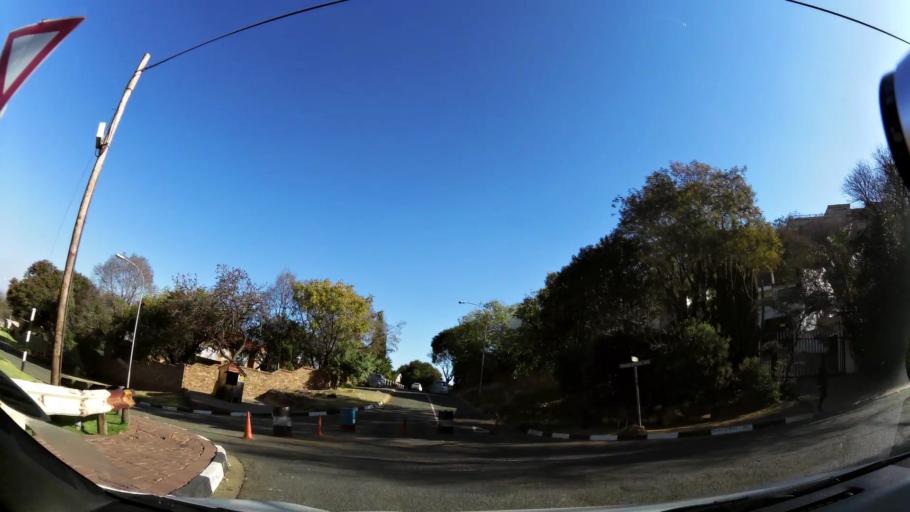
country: ZA
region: Gauteng
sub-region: City of Johannesburg Metropolitan Municipality
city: Johannesburg
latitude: -26.2839
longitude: 28.0498
